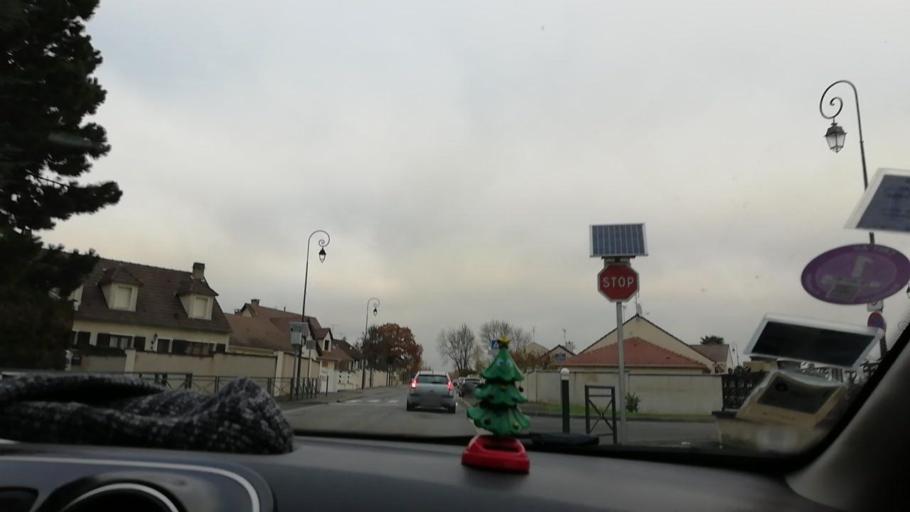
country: FR
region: Ile-de-France
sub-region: Departement de Seine-et-Marne
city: Monthyon
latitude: 49.0071
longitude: 2.8343
